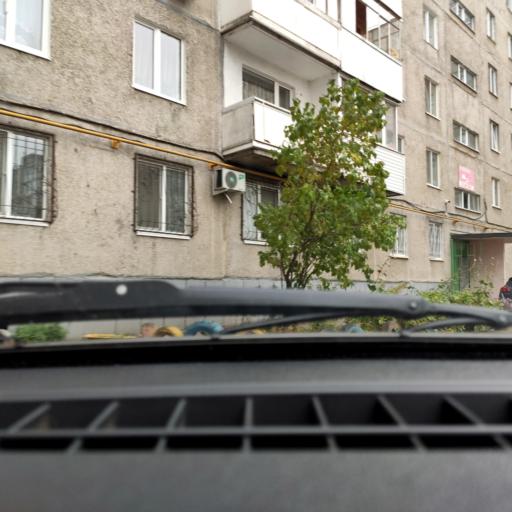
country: RU
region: Bashkortostan
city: Ufa
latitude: 54.7767
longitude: 56.1258
